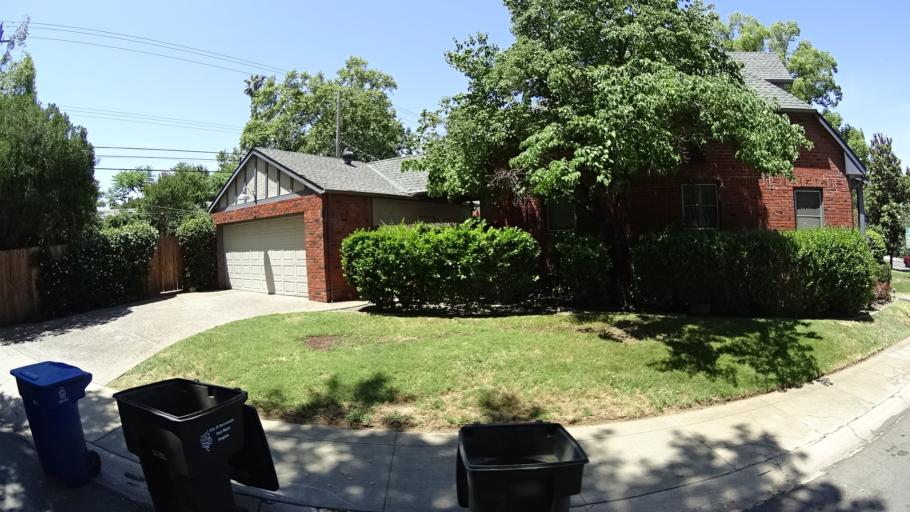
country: US
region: California
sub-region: Sacramento County
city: Sacramento
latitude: 38.5692
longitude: -121.4416
